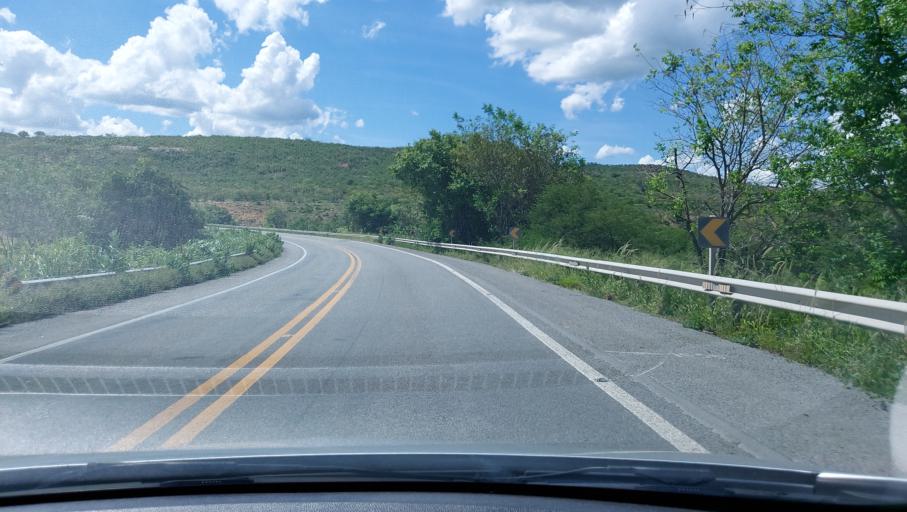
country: BR
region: Bahia
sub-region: Itaberaba
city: Itaberaba
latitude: -12.5093
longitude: -40.4454
